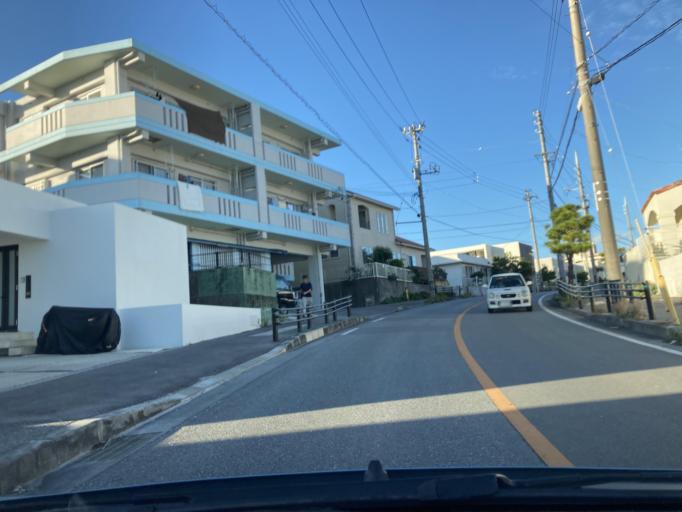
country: JP
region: Okinawa
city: Ginowan
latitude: 26.2537
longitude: 127.7698
